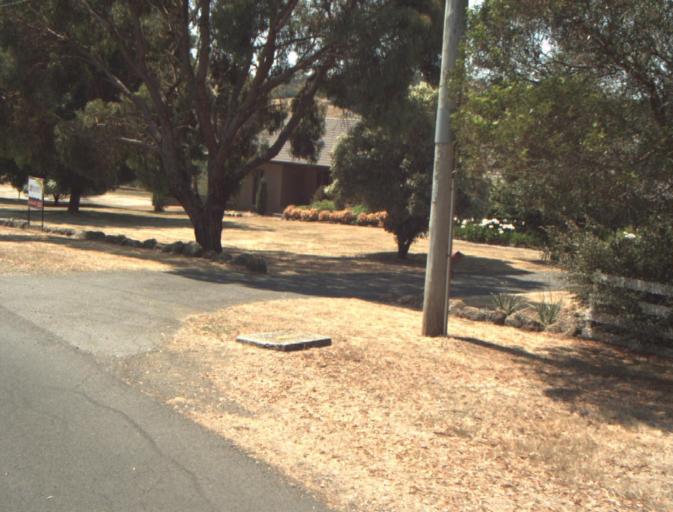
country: AU
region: Tasmania
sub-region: Launceston
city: Newstead
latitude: -41.4902
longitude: 147.1837
